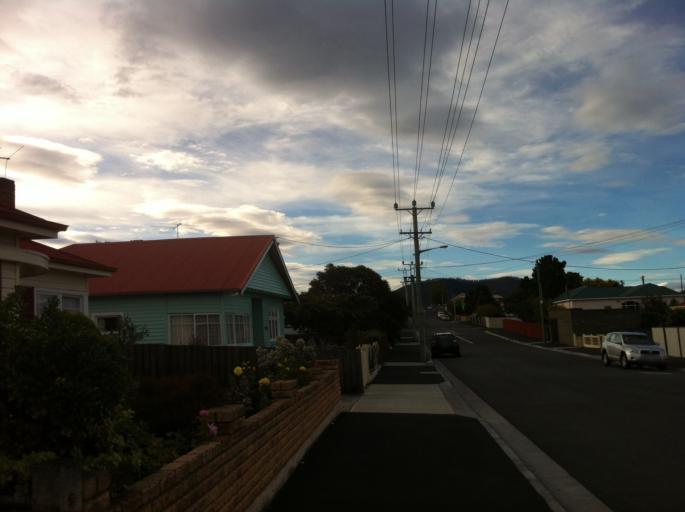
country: AU
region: Tasmania
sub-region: Glenorchy
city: Moonah
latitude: -42.8467
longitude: 147.3044
